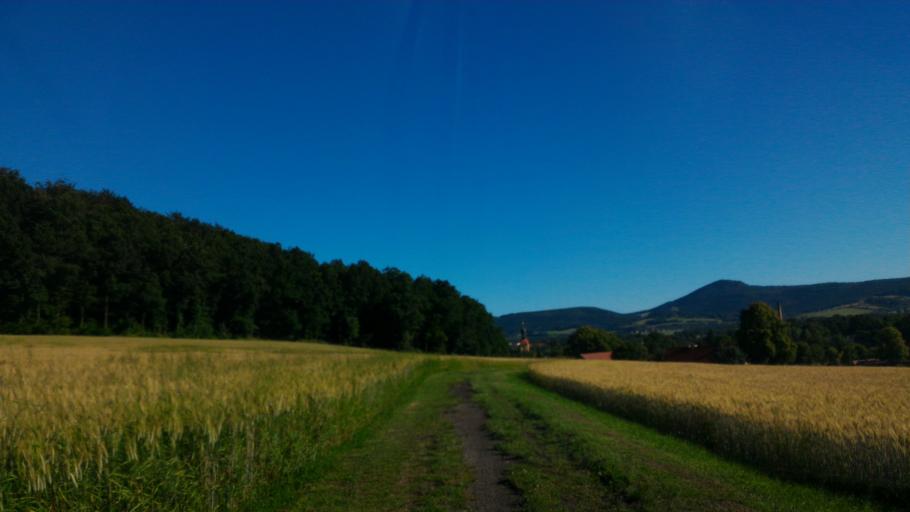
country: DE
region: Saxony
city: Grossschonau
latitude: 50.9036
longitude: 14.6622
